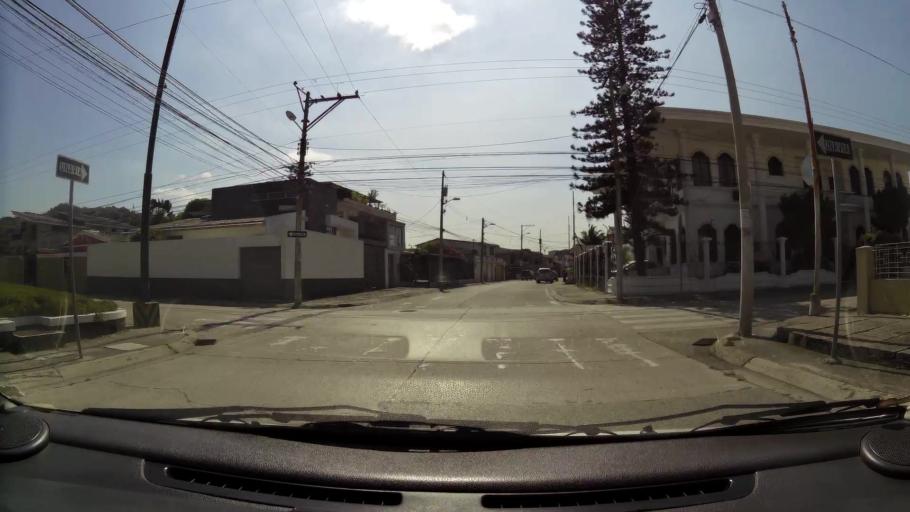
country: EC
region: Guayas
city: Guayaquil
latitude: -2.1750
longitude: -79.9083
